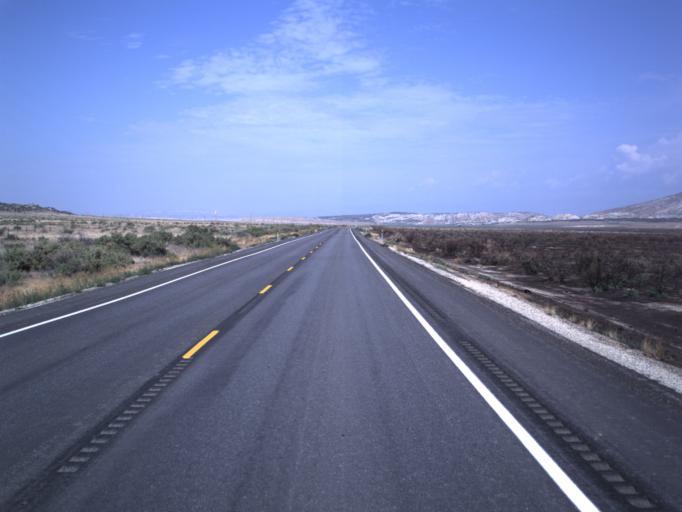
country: US
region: Utah
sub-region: Uintah County
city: Naples
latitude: 40.2940
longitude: -109.1772
